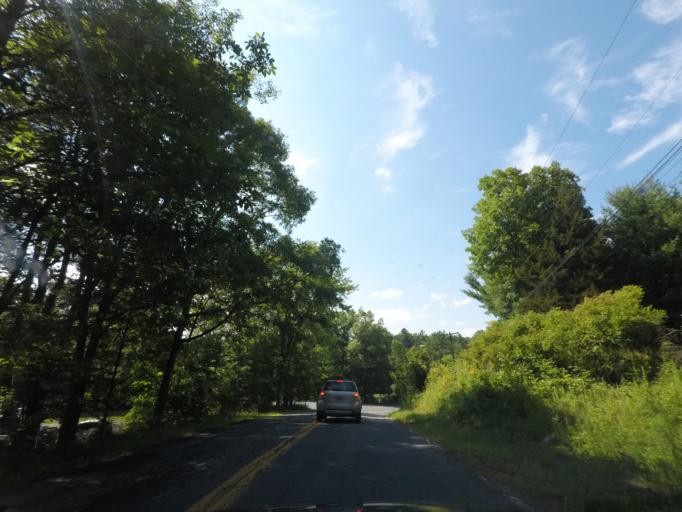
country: US
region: New York
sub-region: Rensselaer County
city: Averill Park
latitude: 42.5819
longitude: -73.5694
